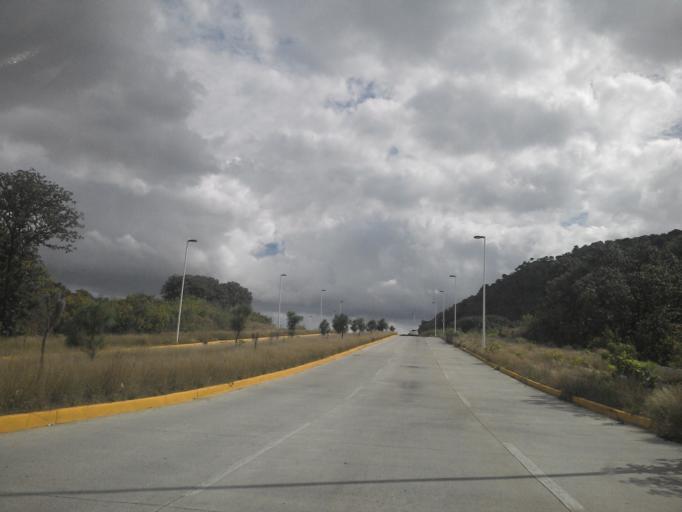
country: MX
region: Jalisco
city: Guadalajara
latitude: 20.6690
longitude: -103.4605
